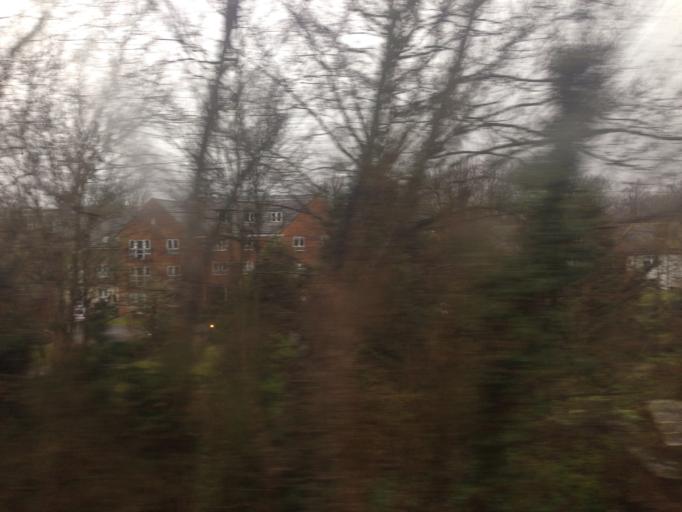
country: GB
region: England
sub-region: Greater London
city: Carshalton
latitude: 51.3702
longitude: -0.1616
